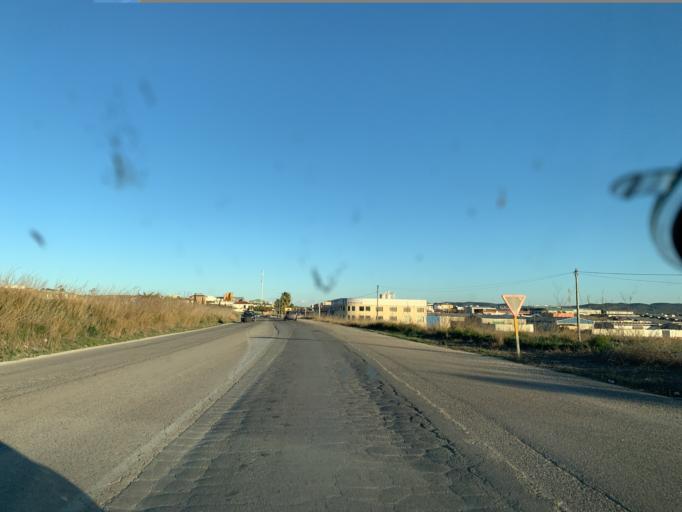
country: ES
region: Andalusia
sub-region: Provincia de Sevilla
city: Pedrera
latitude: 37.2345
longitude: -4.9040
